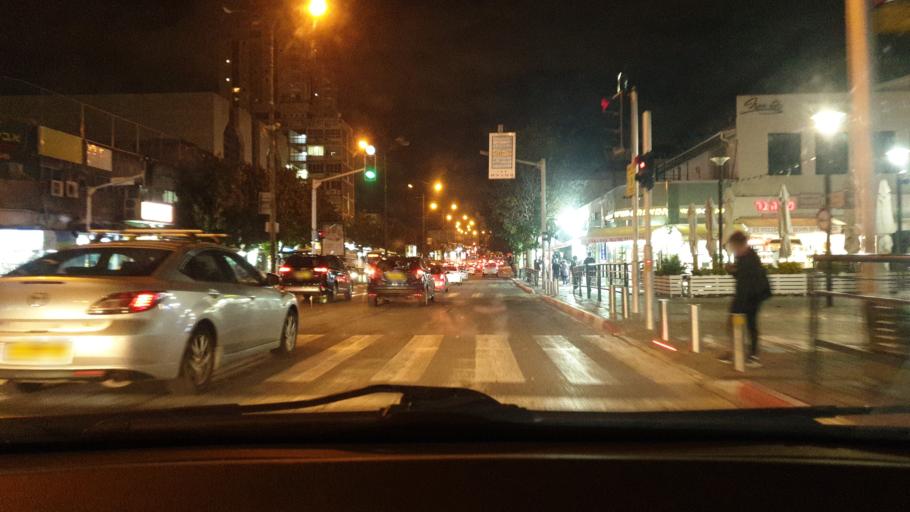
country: IL
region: Central District
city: Rishon LeZiyyon
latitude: 31.9639
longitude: 34.8031
